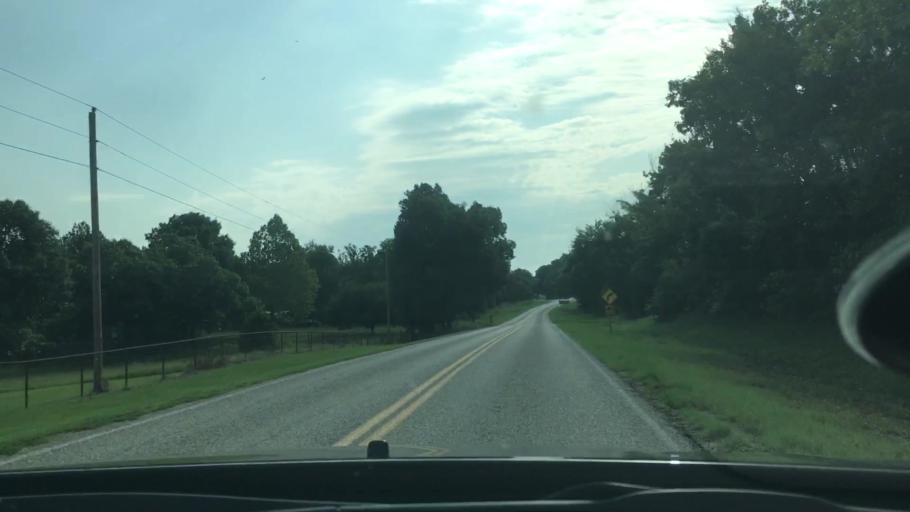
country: US
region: Oklahoma
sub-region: Johnston County
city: Tishomingo
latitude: 34.2087
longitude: -96.5878
